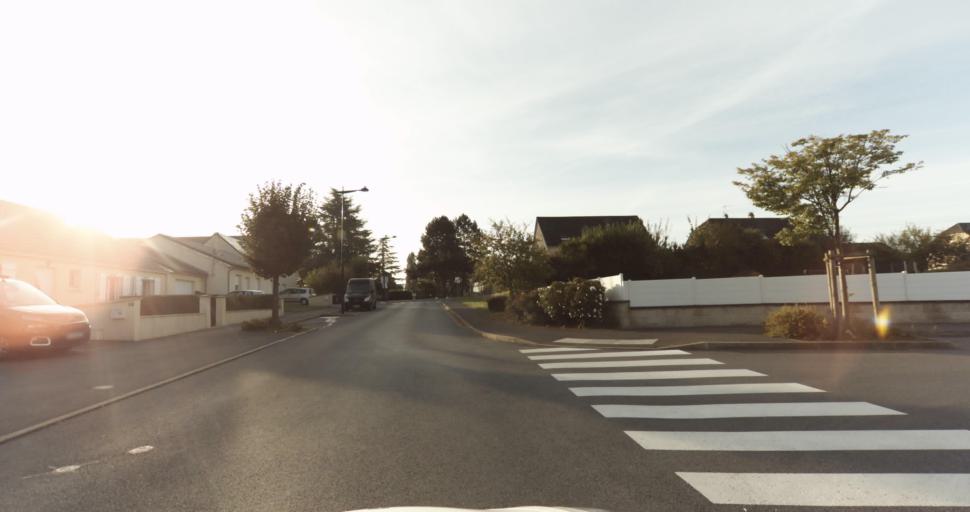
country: FR
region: Champagne-Ardenne
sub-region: Departement des Ardennes
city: Villers-Semeuse
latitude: 49.7376
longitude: 4.7434
